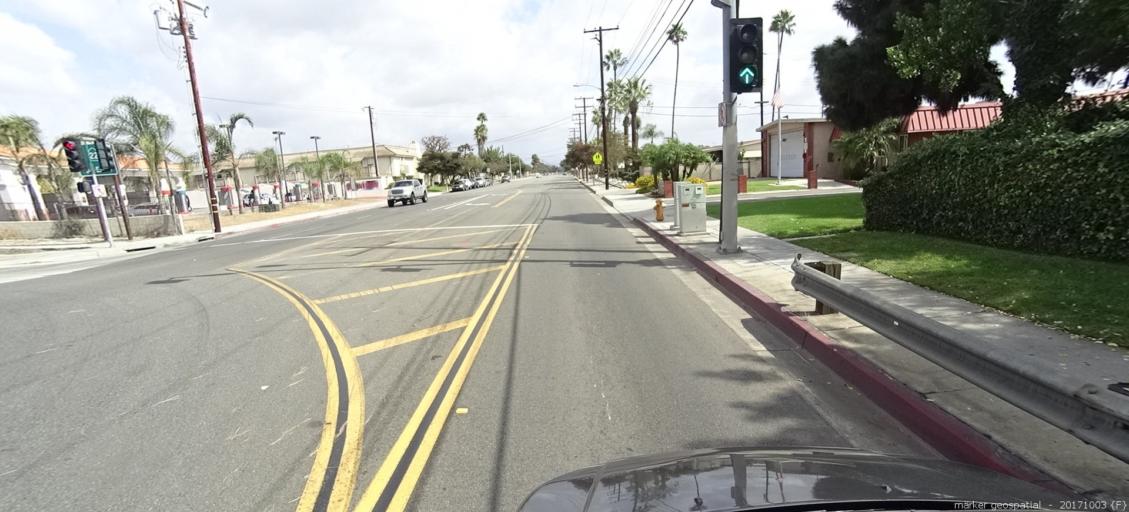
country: US
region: California
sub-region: Orange County
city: Garden Grove
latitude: 33.7670
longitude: -117.9182
